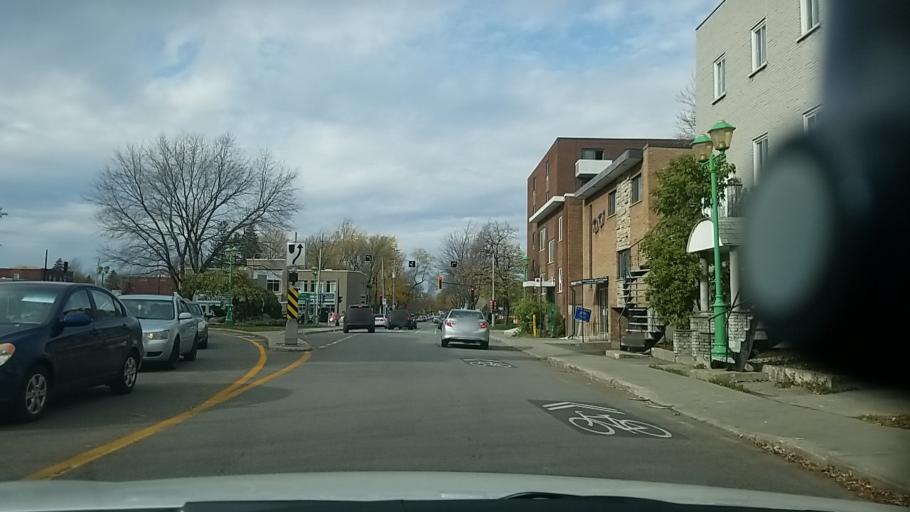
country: CA
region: Quebec
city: Saint-Laurent
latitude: 45.5157
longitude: -73.6791
